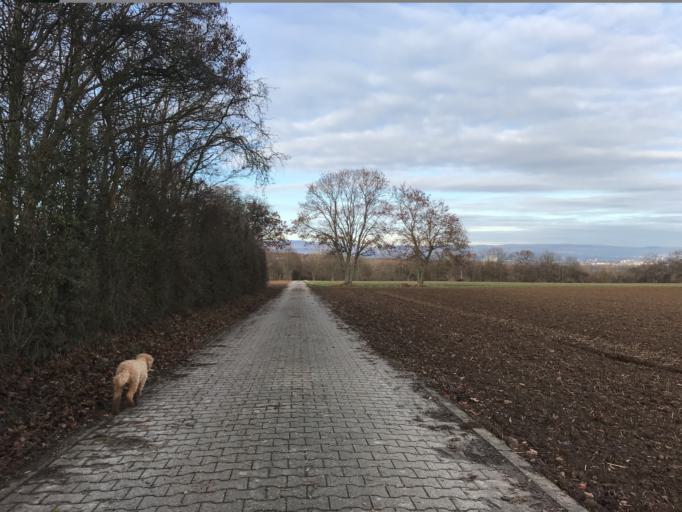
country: DE
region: Rheinland-Pfalz
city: Klein-Winternheim
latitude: 49.9692
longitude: 8.2071
